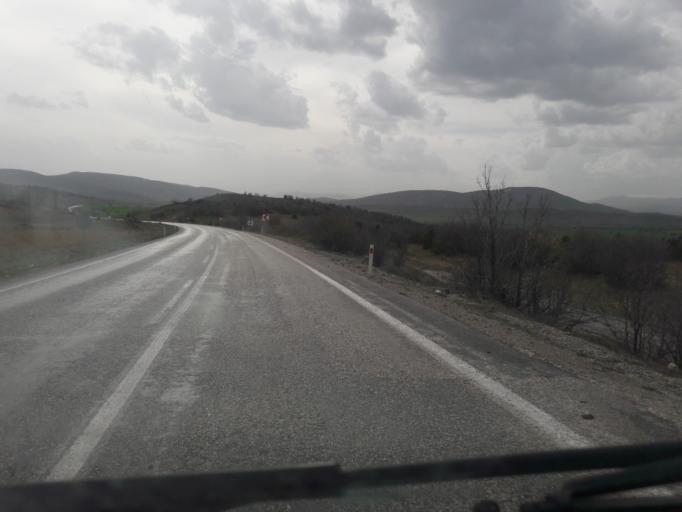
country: TR
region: Gumushane
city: Evren
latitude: 40.1714
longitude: 39.2343
